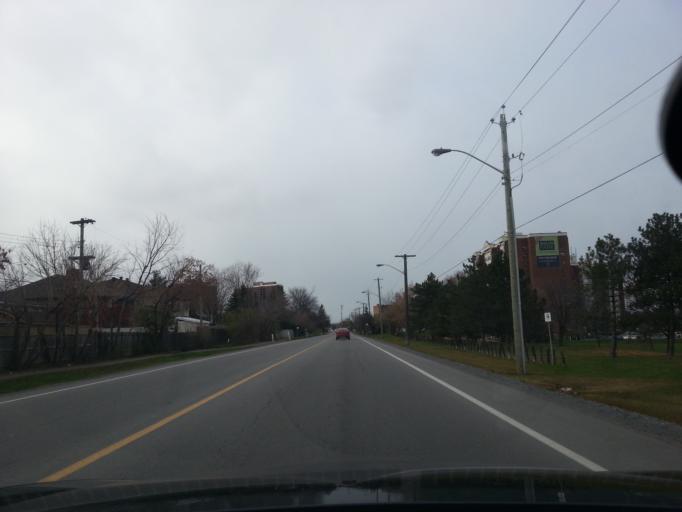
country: CA
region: Ontario
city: Ottawa
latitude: 45.3960
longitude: -75.6142
